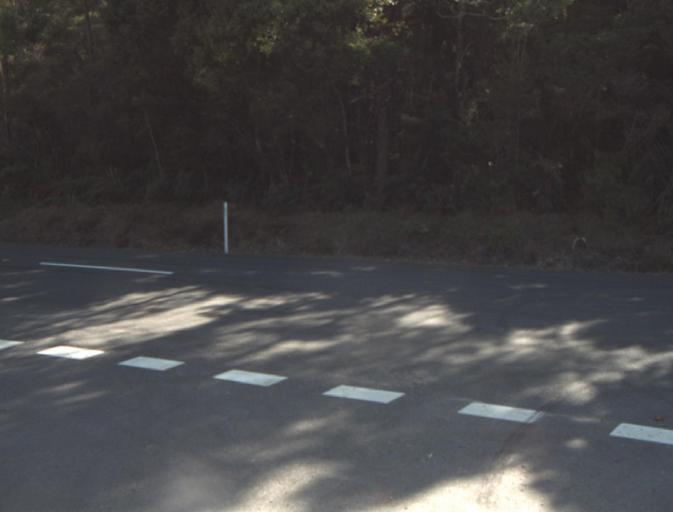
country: AU
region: Tasmania
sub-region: Dorset
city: Bridport
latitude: -41.1600
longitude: 147.2388
